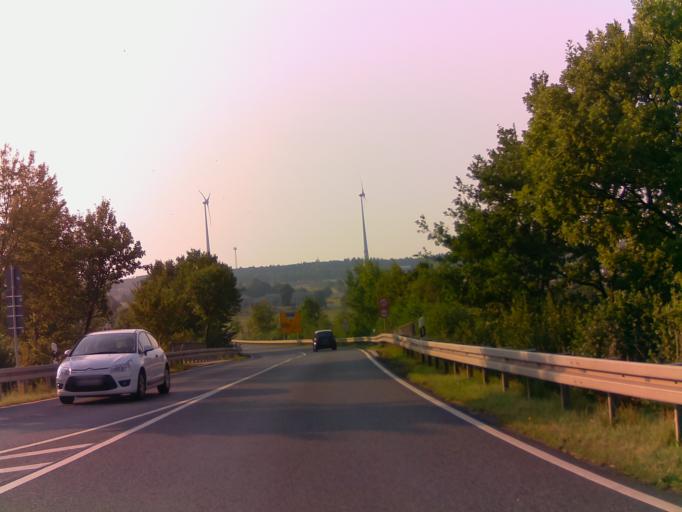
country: DE
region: Hesse
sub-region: Regierungsbezirk Kassel
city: Friedewald
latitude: 50.8824
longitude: 9.8695
